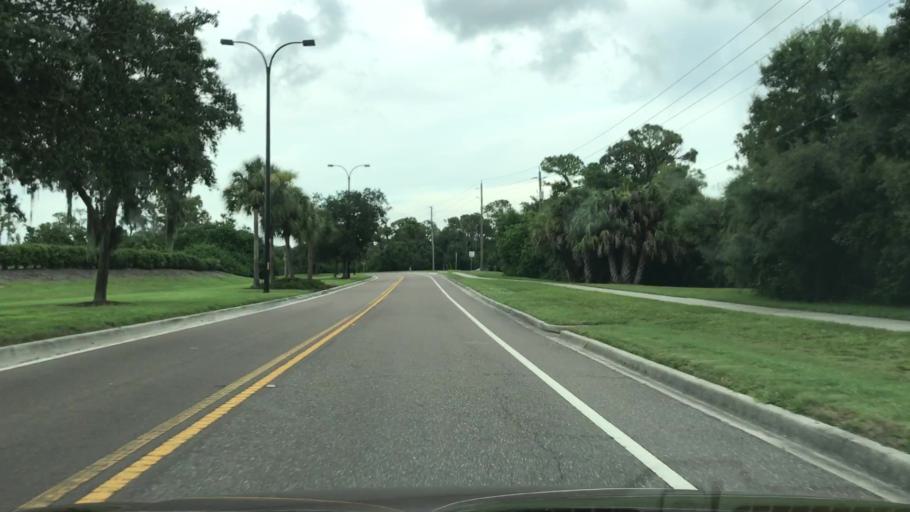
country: US
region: Florida
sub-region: Sarasota County
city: Vamo
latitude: 27.2380
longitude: -82.4774
